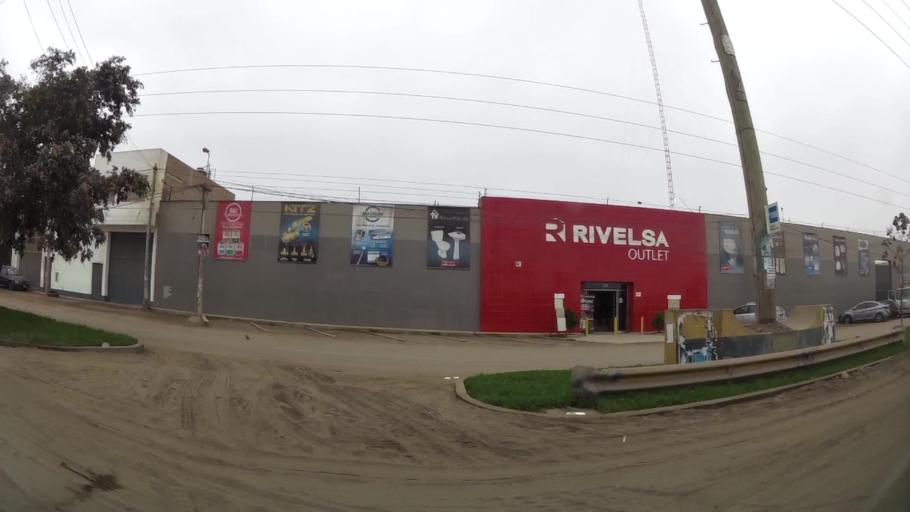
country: PE
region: Lima
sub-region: Lima
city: Punta Hermosa
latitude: -12.2576
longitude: -76.8877
